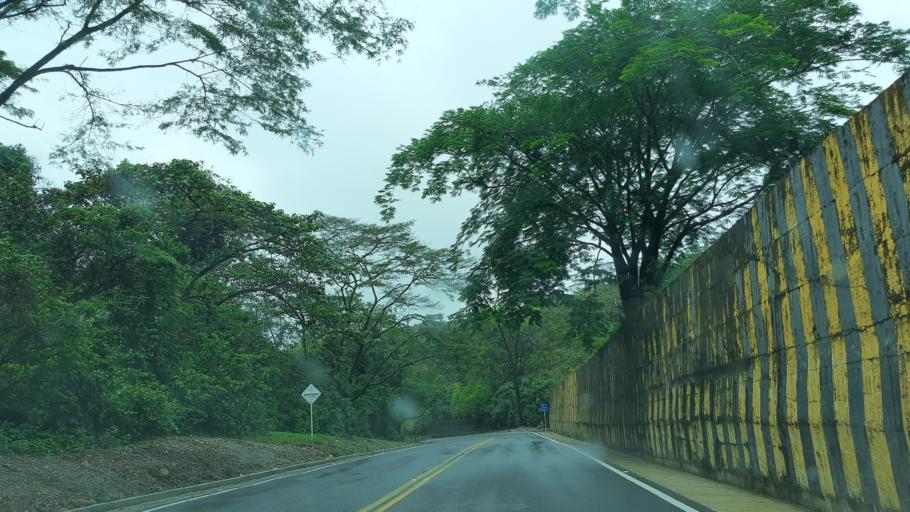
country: CO
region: Casanare
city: Sabanalarga
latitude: 4.7582
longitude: -73.0224
